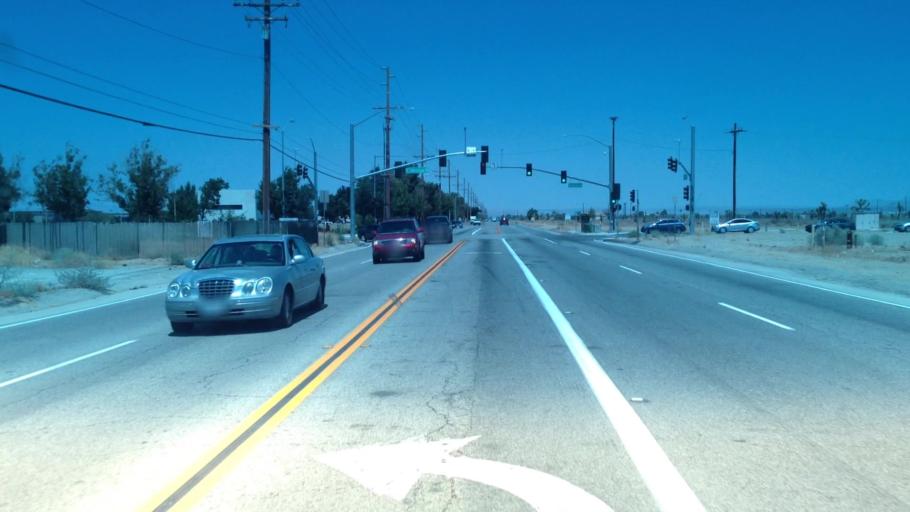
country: US
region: California
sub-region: Los Angeles County
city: Desert View Highlands
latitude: 34.6304
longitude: -118.1477
